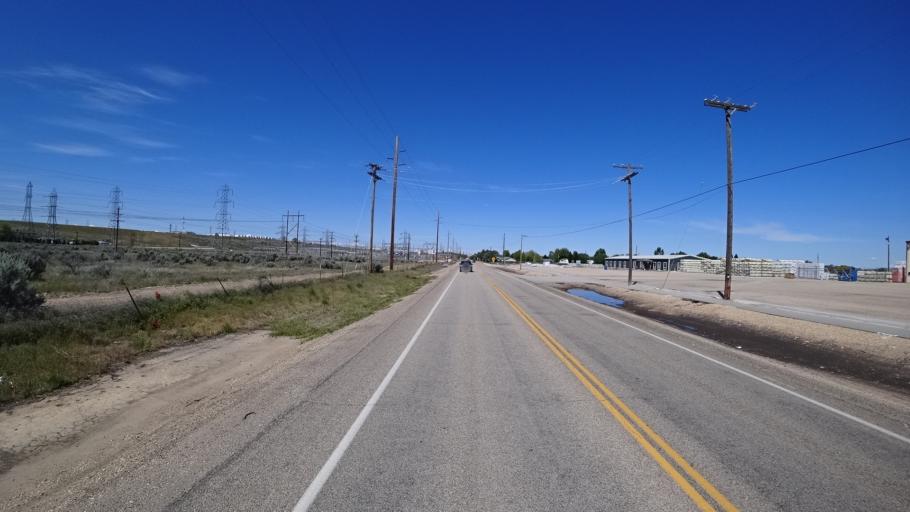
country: US
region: Idaho
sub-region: Ada County
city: Boise
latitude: 43.5603
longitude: -116.1504
